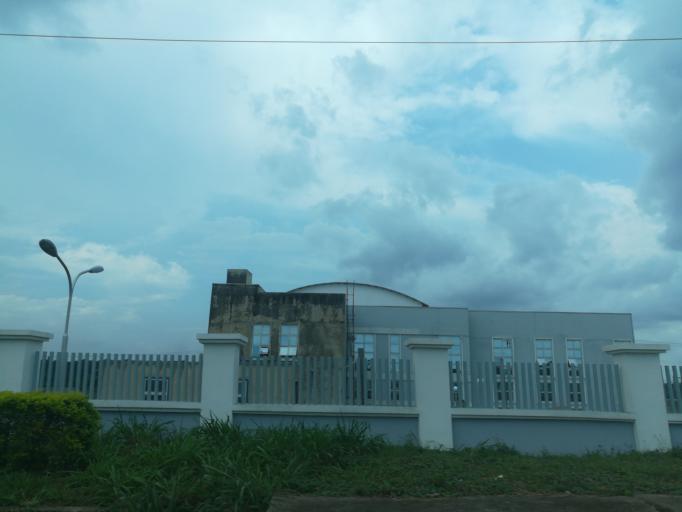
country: NG
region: Lagos
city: Ikorodu
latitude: 6.6367
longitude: 3.5345
